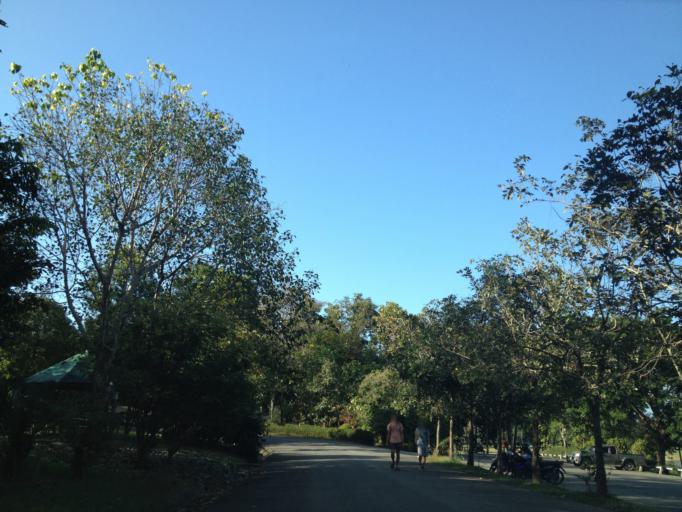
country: TH
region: Chiang Mai
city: Chiang Mai
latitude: 18.8649
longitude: 98.9390
